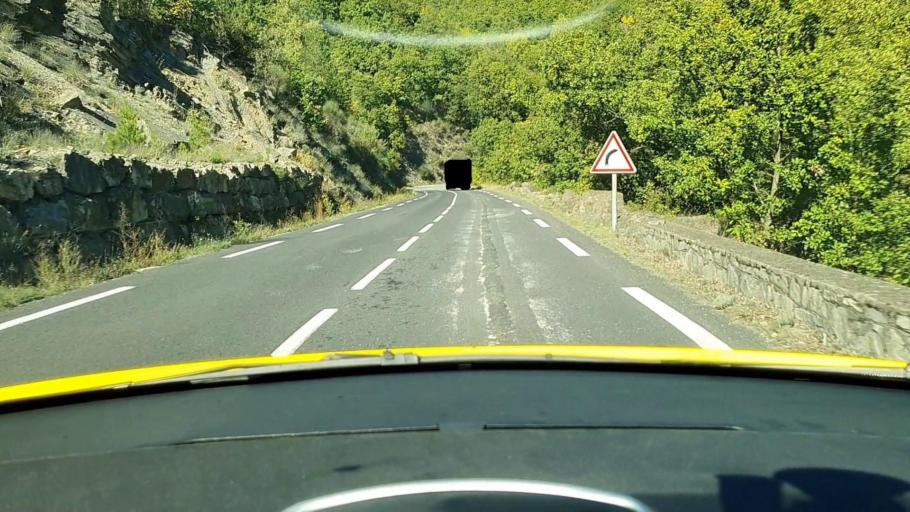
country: FR
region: Languedoc-Roussillon
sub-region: Departement du Gard
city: Le Vigan
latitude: 43.9757
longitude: 3.4610
